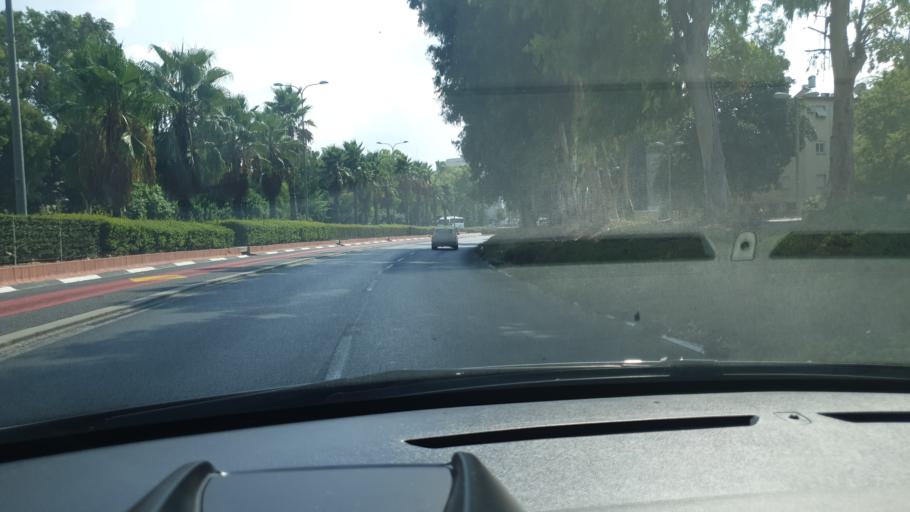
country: IL
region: Haifa
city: Qiryat Bialik
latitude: 32.8195
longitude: 35.0790
